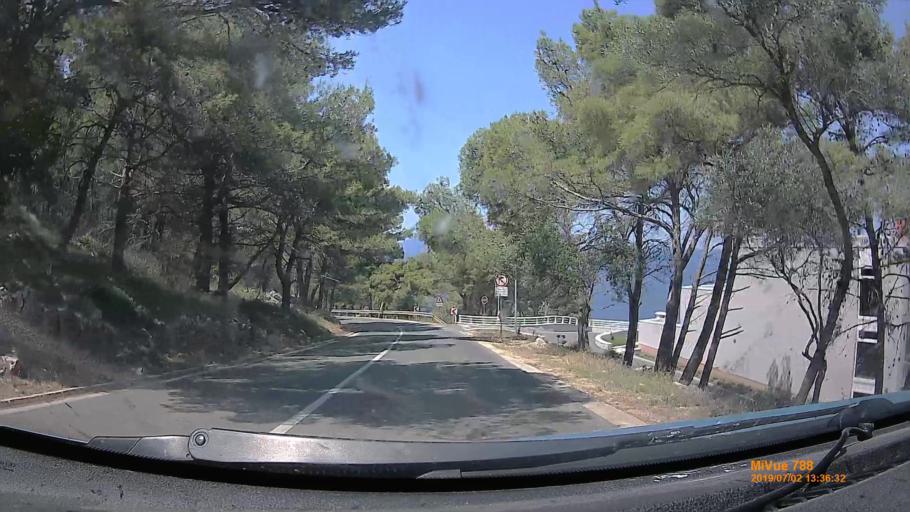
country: HR
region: Primorsko-Goranska
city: Mali Losinj
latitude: 44.5238
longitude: 14.4952
